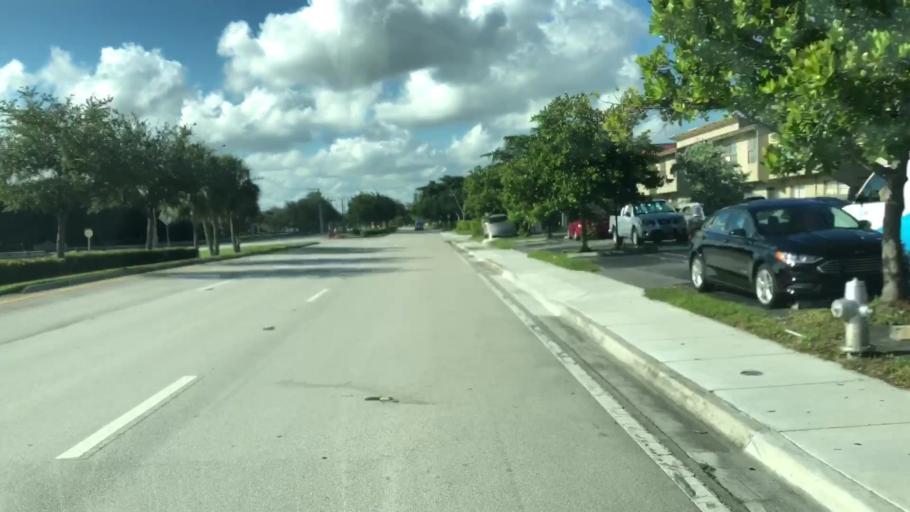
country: US
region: Florida
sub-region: Broward County
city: Coral Springs
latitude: 26.2627
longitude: -80.2663
